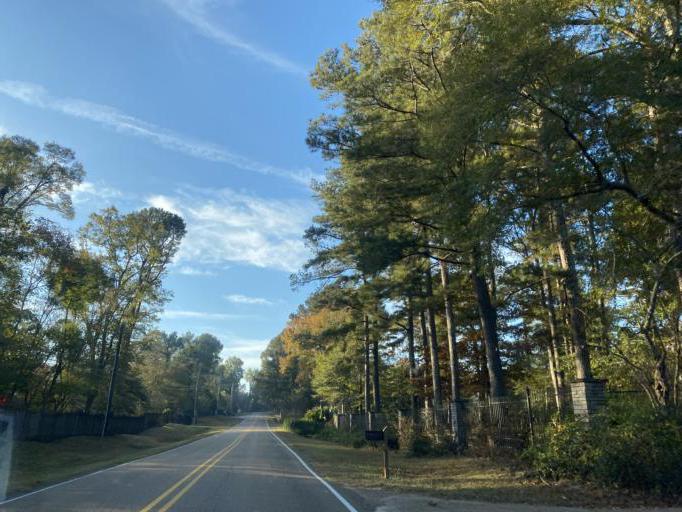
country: US
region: Mississippi
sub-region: Madison County
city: Madison
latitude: 32.4678
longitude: -90.0721
